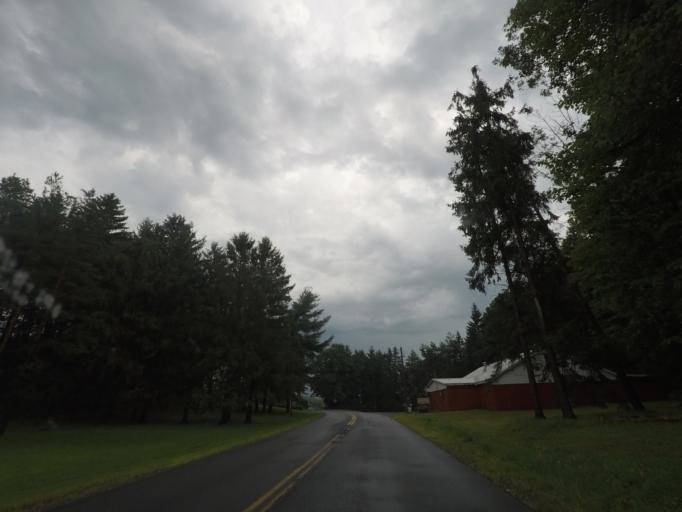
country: US
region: New York
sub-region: Rensselaer County
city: Poestenkill
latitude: 42.7235
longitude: -73.5850
